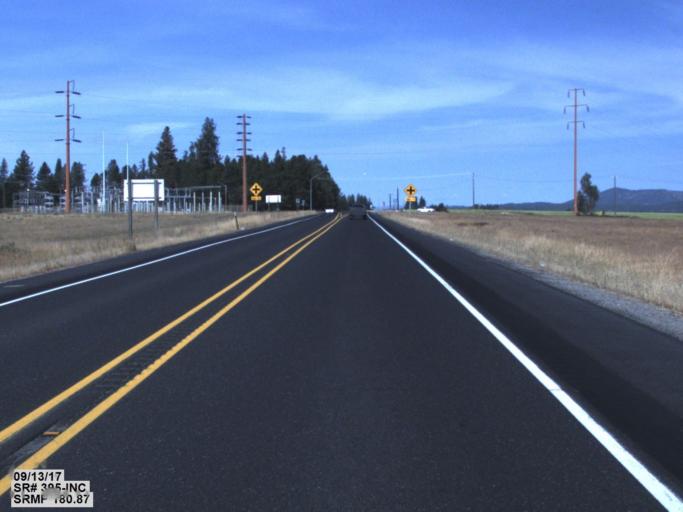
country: US
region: Washington
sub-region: Spokane County
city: Deer Park
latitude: 47.9587
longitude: -117.4936
